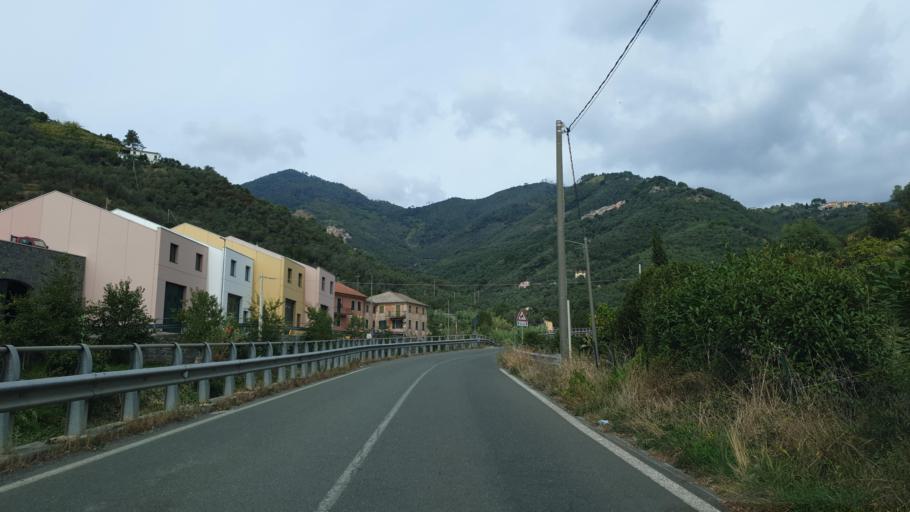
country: IT
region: Liguria
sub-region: Provincia di La Spezia
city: Levanto
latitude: 44.1830
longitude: 9.6210
